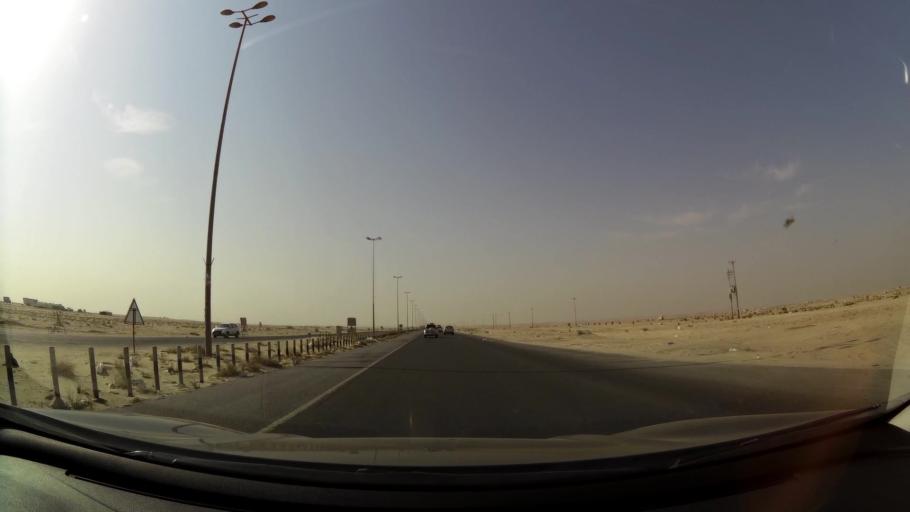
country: KW
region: Al Ahmadi
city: Al Ahmadi
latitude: 28.8839
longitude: 48.0819
